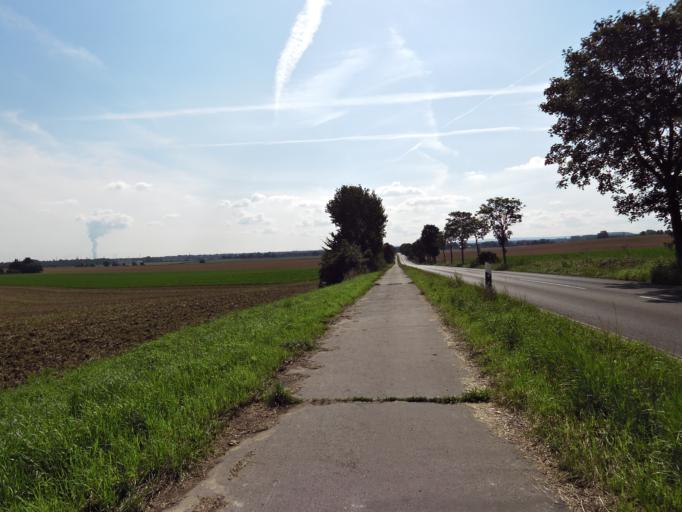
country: NL
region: Limburg
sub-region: Gemeente Kerkrade
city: Kerkrade
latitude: 50.8431
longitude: 6.0251
